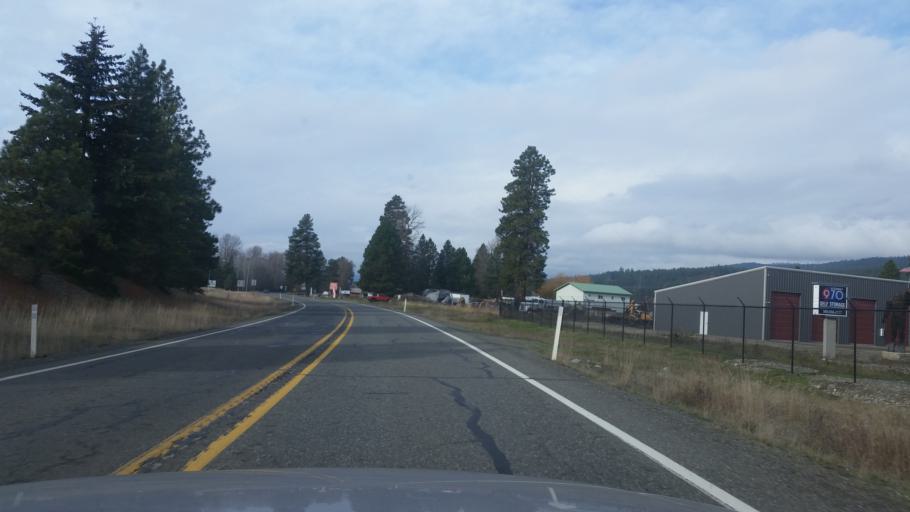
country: US
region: Washington
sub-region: Kittitas County
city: Cle Elum
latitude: 47.1880
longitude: -120.8997
